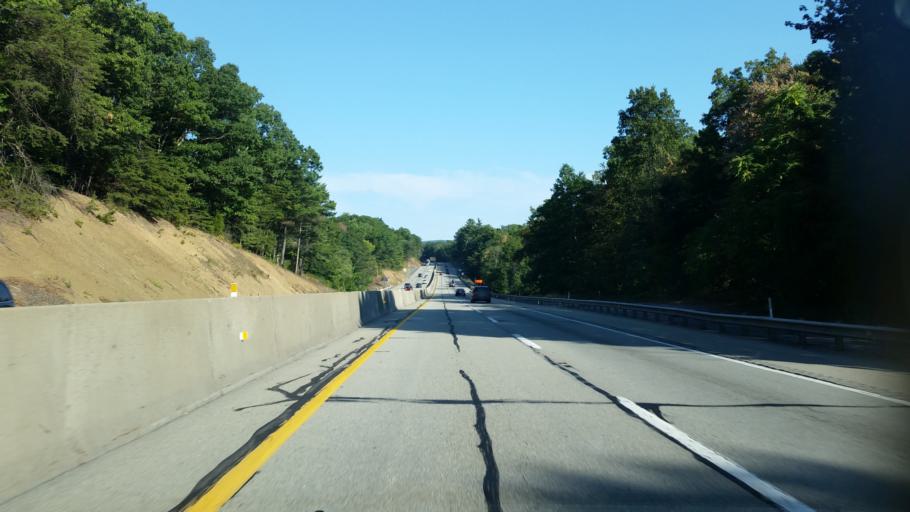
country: US
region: Pennsylvania
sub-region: Fulton County
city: McConnellsburg
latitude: 40.0412
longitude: -78.0110
